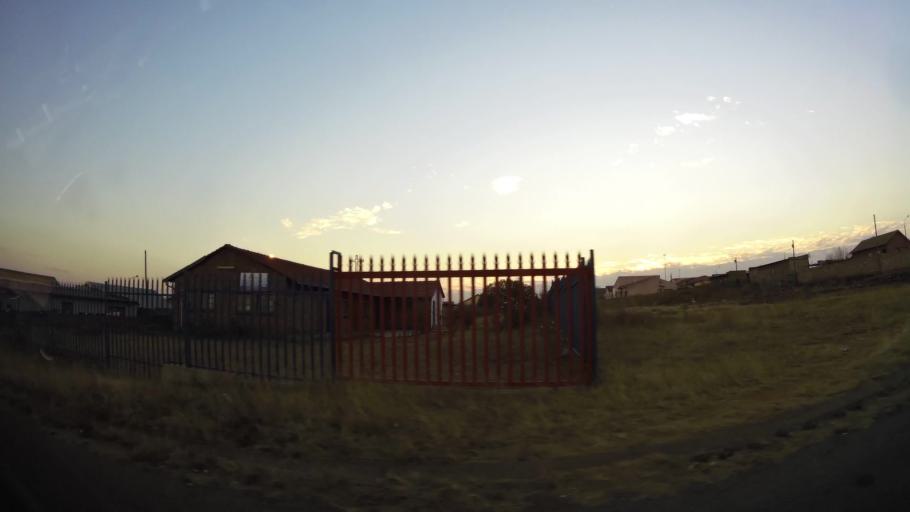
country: ZA
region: Gauteng
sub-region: West Rand District Municipality
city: Randfontein
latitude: -26.2096
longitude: 27.7189
